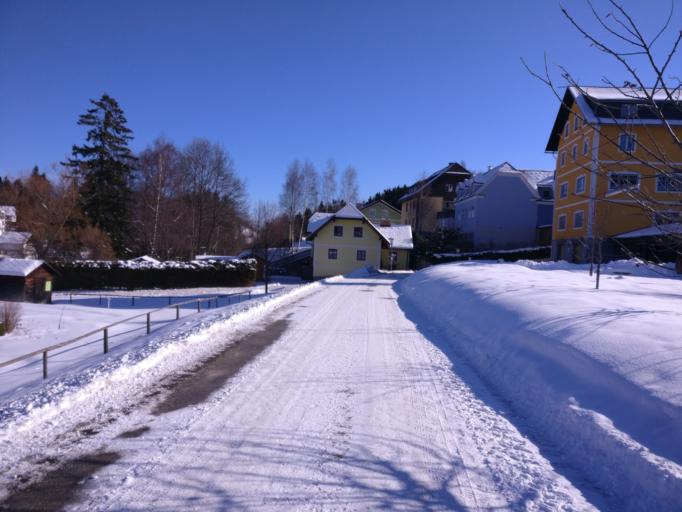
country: AT
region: Styria
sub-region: Politischer Bezirk Hartberg-Fuerstenfeld
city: Sankt Jakob im Walde
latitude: 47.4674
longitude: 15.7881
